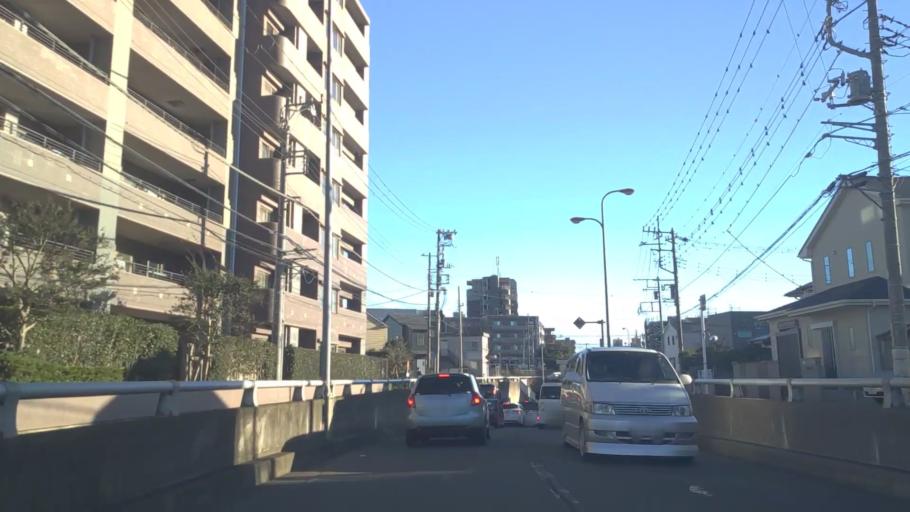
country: JP
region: Kanagawa
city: Chigasaki
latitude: 35.3343
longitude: 139.4149
